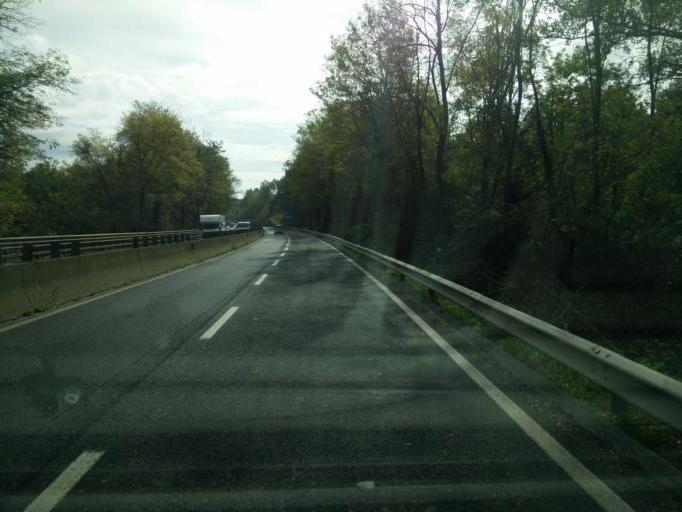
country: IT
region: Tuscany
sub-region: Provincia di Siena
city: Siena
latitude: 43.3182
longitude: 11.3018
